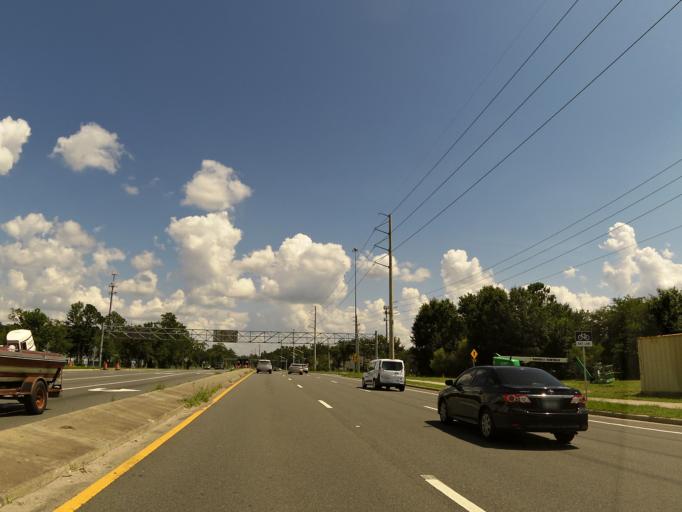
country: US
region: Florida
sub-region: Saint Johns County
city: Fruit Cove
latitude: 30.1687
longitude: -81.6023
